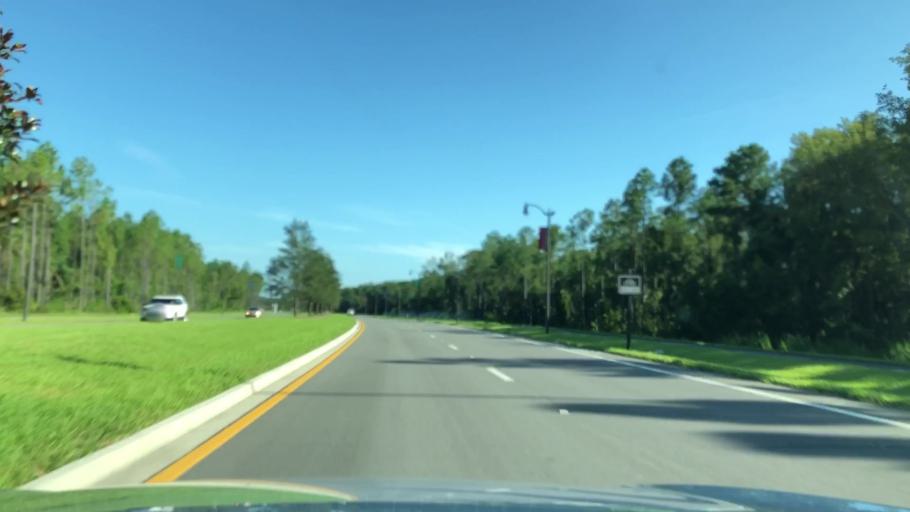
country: US
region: Florida
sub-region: Saint Johns County
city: Palm Valley
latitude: 30.0880
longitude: -81.4057
